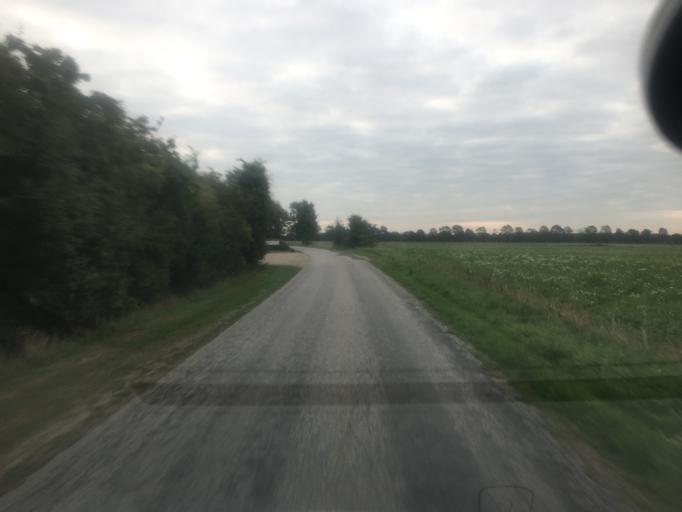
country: DK
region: South Denmark
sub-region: Tonder Kommune
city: Logumkloster
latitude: 55.0371
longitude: 8.9884
